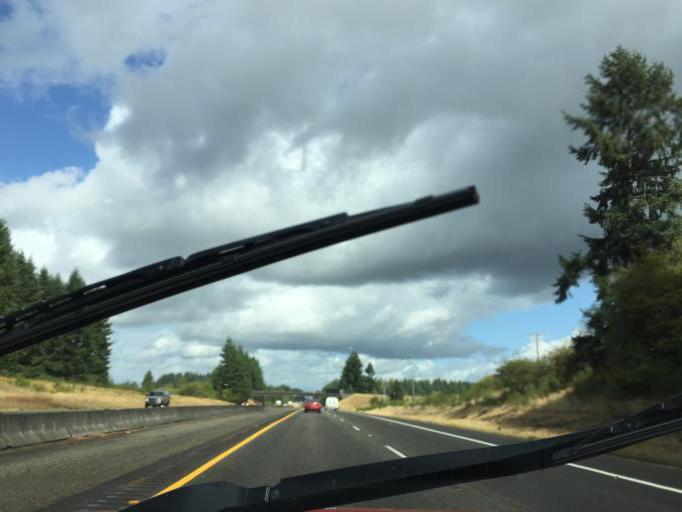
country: US
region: Washington
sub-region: Lewis County
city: Winlock
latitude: 46.5148
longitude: -122.8766
